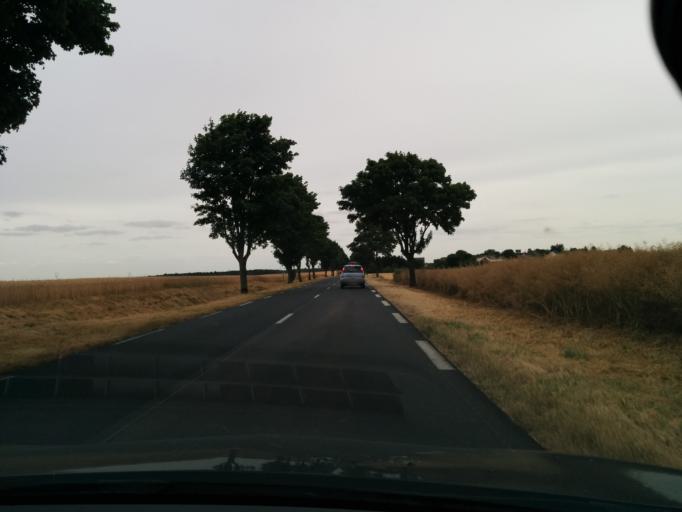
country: FR
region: Ile-de-France
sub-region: Departement de l'Essonne
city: Pussay
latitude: 48.3802
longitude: 1.9771
